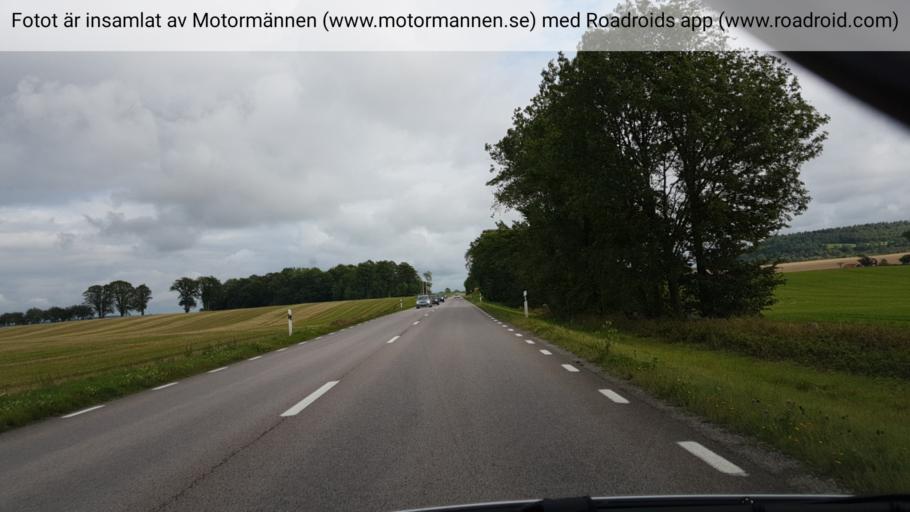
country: SE
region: Vaestra Goetaland
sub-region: Falkopings Kommun
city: Falkoeping
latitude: 58.1568
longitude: 13.5852
